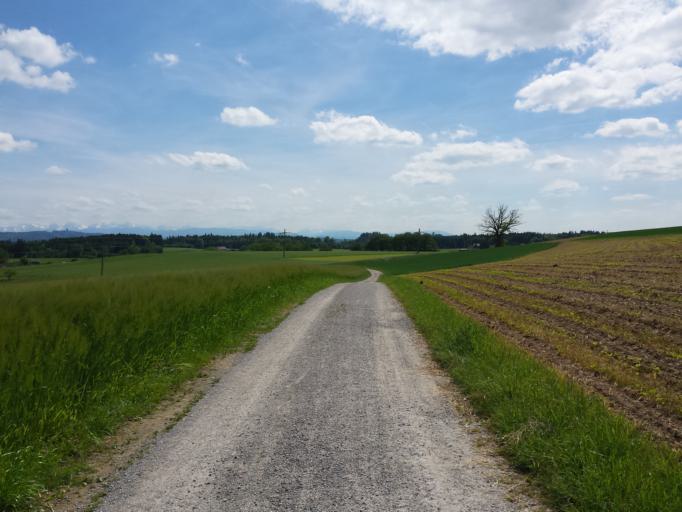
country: CH
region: Bern
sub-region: Bern-Mittelland District
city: Kirchlindach
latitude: 47.0005
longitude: 7.4240
